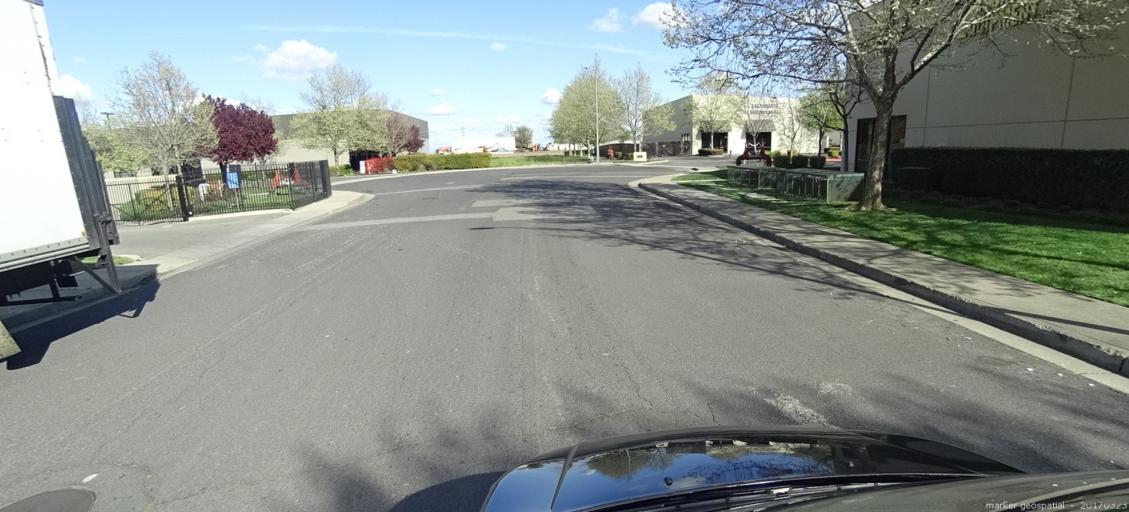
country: US
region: California
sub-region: Sacramento County
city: Rosemont
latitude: 38.5164
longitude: -121.3686
